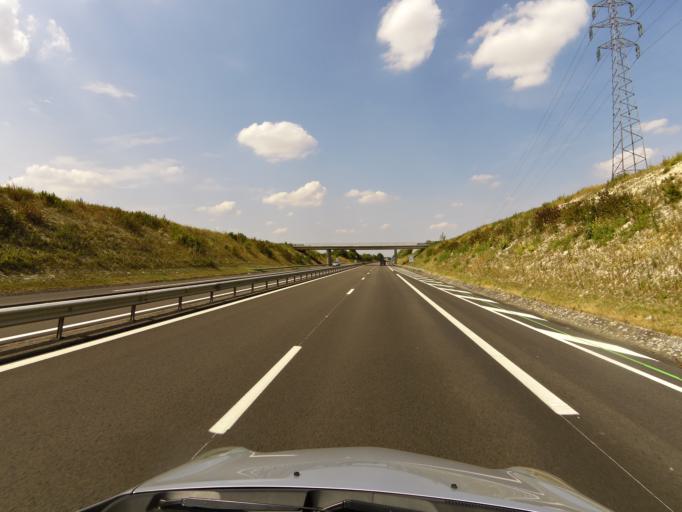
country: FR
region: Champagne-Ardenne
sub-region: Departement de la Marne
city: Loivre
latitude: 49.3428
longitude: 3.9640
